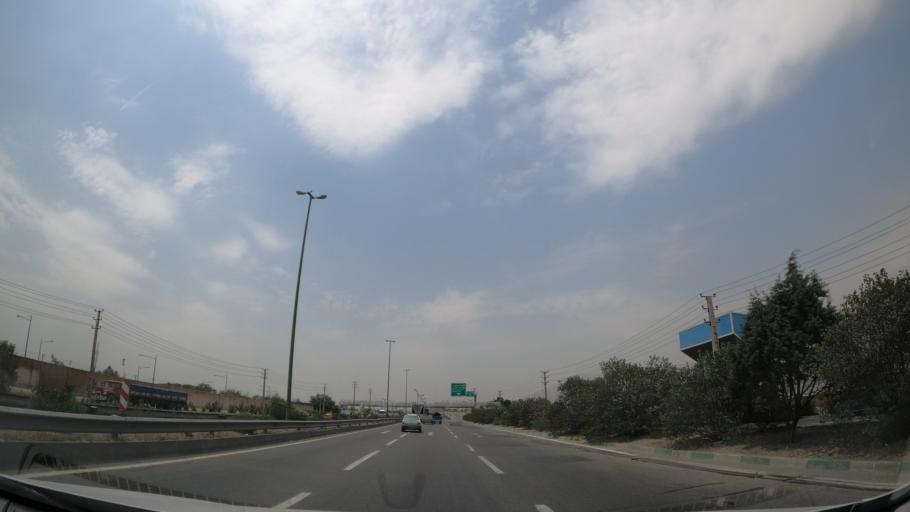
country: IR
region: Tehran
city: Shahr-e Qods
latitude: 35.7015
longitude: 51.1884
